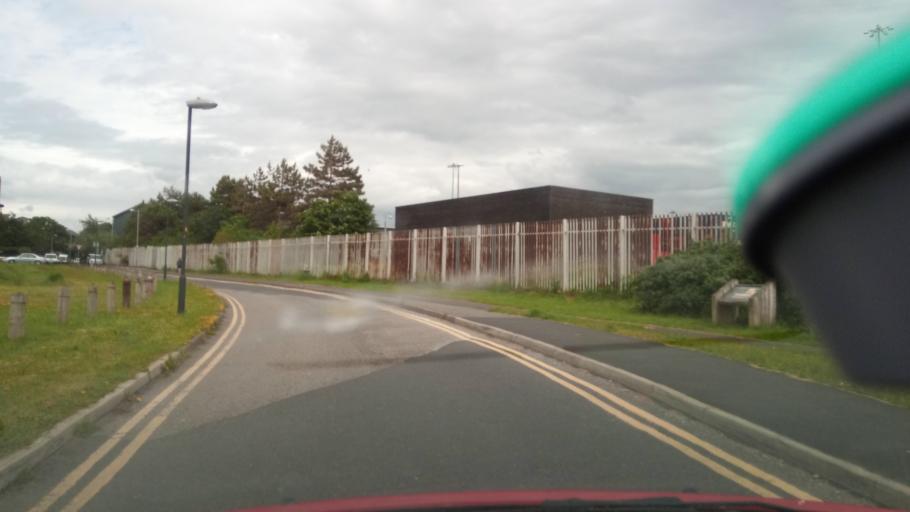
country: GB
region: England
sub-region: Sefton
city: Waterloo
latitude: 53.4685
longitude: -3.0251
